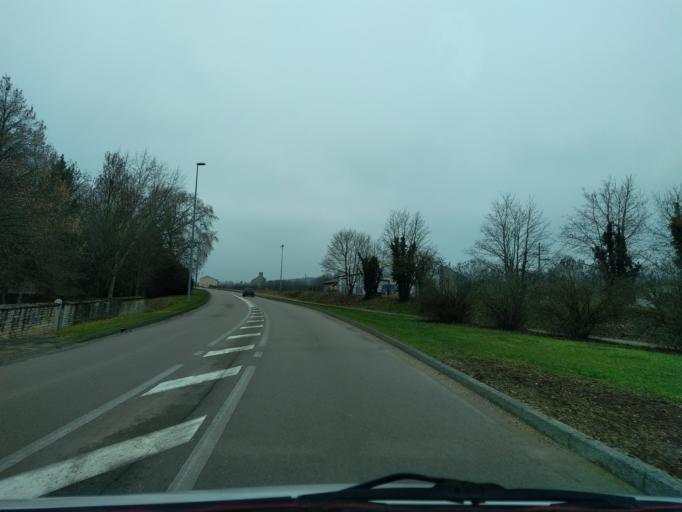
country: FR
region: Franche-Comte
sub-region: Departement de la Haute-Saone
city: Arc-les-Gray
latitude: 47.4530
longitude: 5.5835
